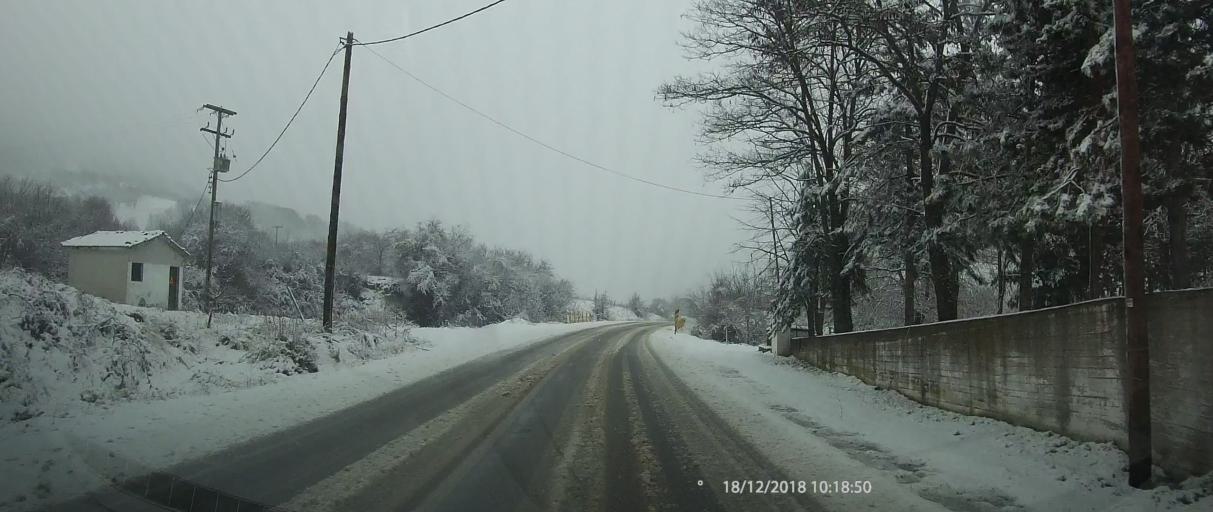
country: GR
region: Thessaly
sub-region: Nomos Larisis
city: Livadi
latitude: 40.1348
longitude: 22.2194
